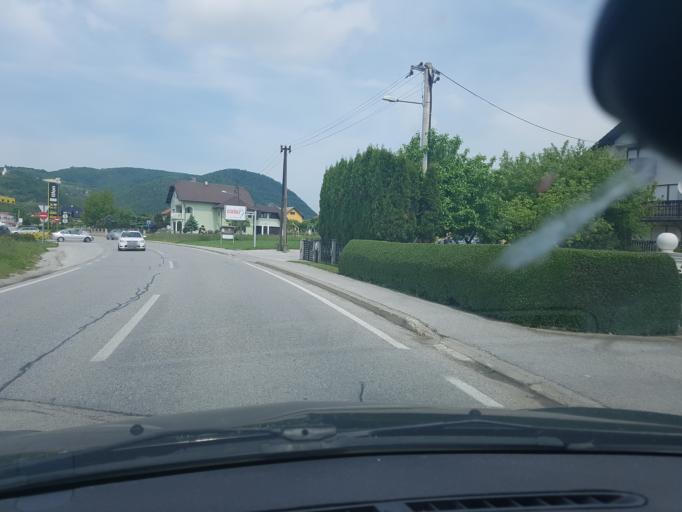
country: HR
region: Krapinsko-Zagorska
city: Pregrada
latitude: 46.1517
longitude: 15.7598
